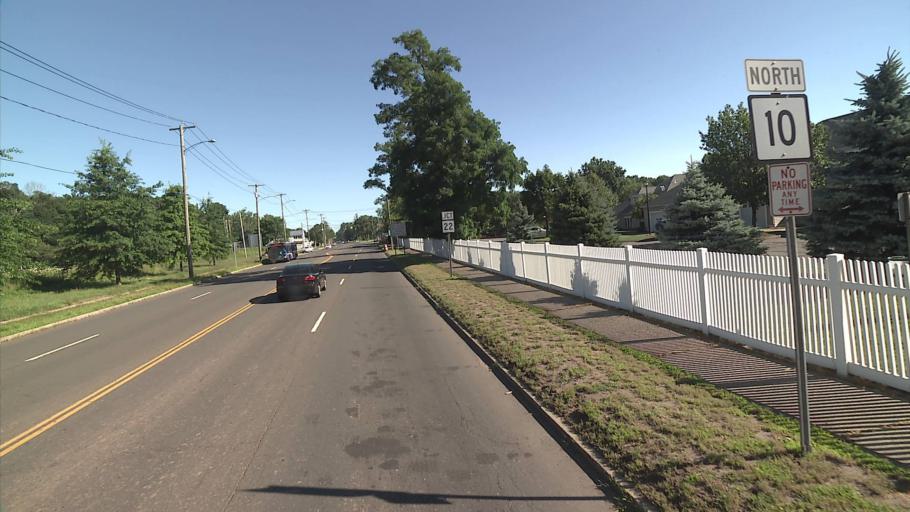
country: US
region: Connecticut
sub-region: New Haven County
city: Hamden
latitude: 41.4024
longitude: -72.8979
